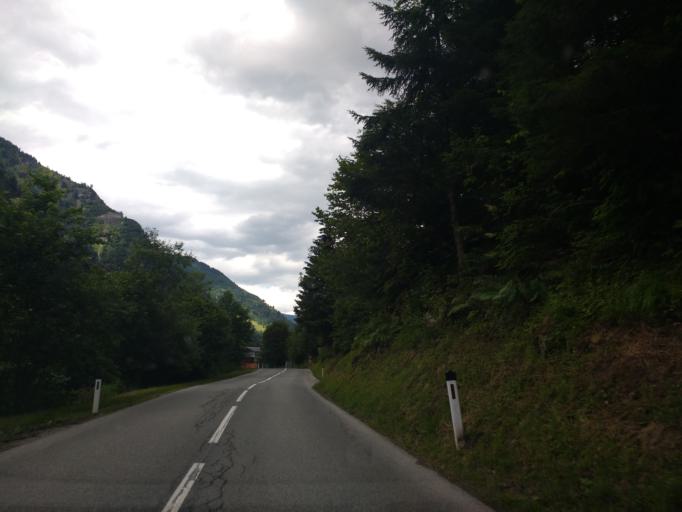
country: AT
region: Salzburg
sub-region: Politischer Bezirk Zell am See
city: Kaprun
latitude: 47.2271
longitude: 12.7265
